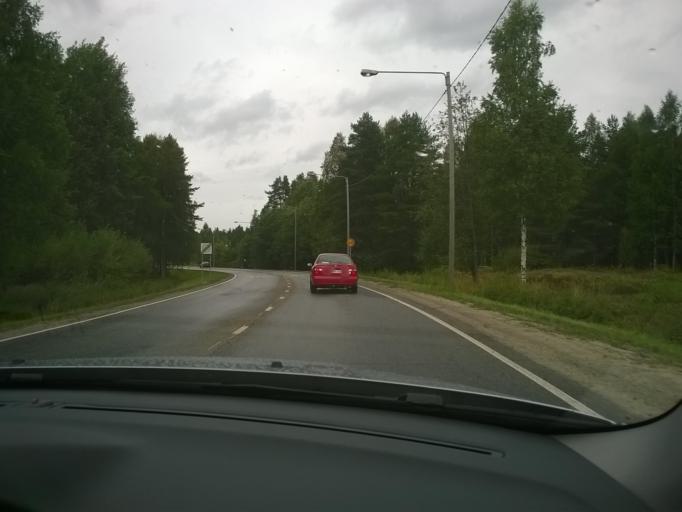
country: FI
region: Kainuu
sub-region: Kehys-Kainuu
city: Kuhmo
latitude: 64.1287
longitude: 29.5018
